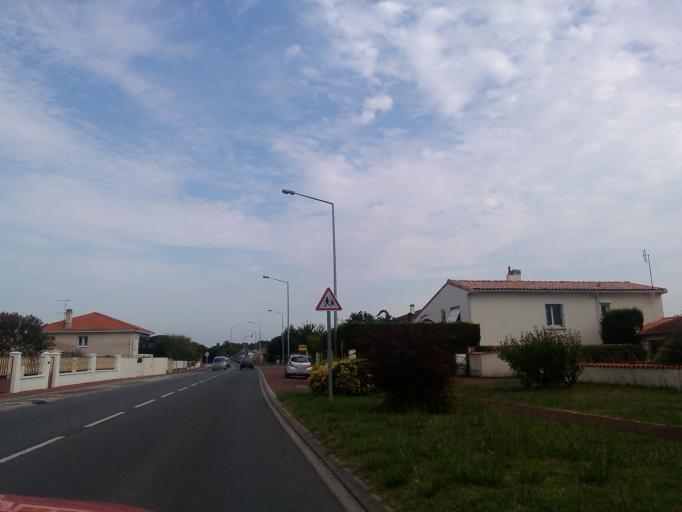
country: FR
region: Poitou-Charentes
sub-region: Departement de la Charente-Maritime
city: Saujon
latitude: 45.6746
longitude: -0.9443
